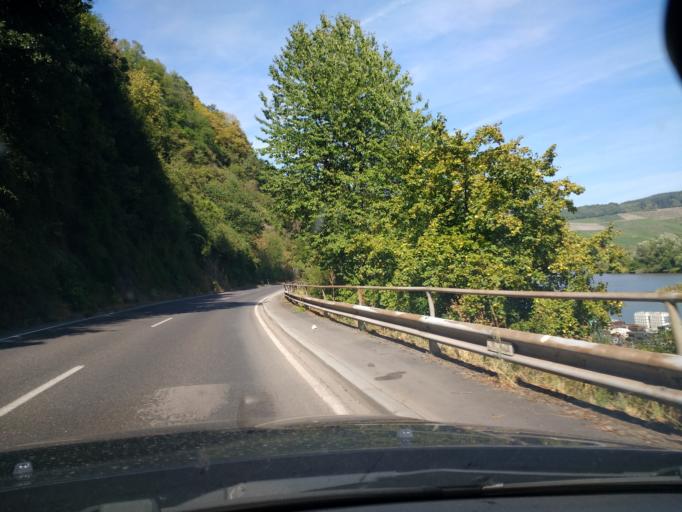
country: DE
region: Rheinland-Pfalz
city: Ayl
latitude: 49.6189
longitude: 6.5603
